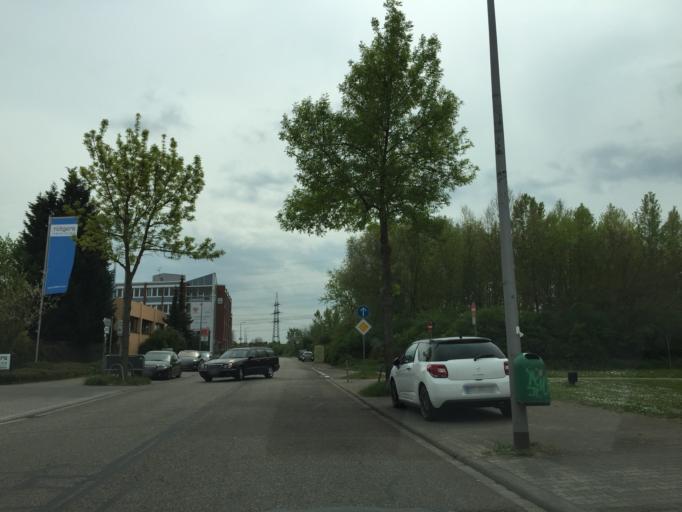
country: DE
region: Rheinland-Pfalz
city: Altrip
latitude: 49.4513
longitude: 8.5139
